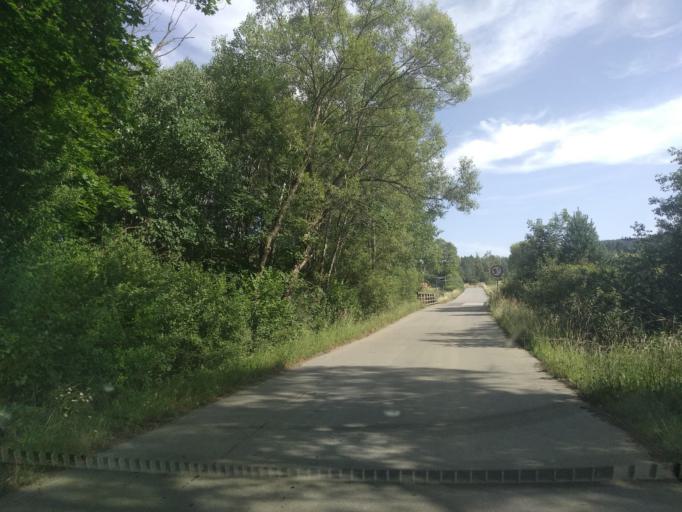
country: PL
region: Subcarpathian Voivodeship
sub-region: Powiat krosnienski
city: Jasliska
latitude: 49.4187
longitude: 21.8565
